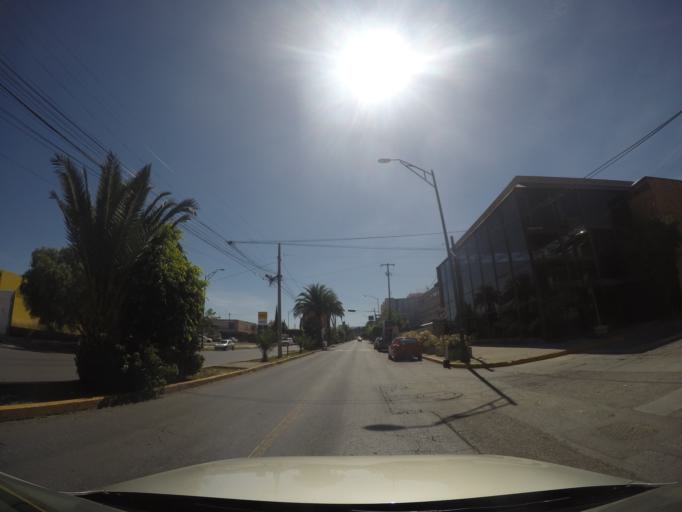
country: MX
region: San Luis Potosi
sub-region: San Luis Potosi
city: San Luis Potosi
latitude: 22.1489
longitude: -101.0093
